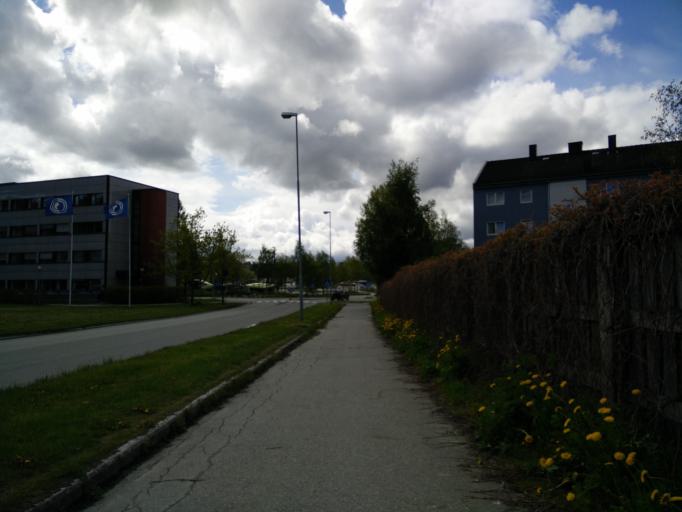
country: NO
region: Sor-Trondelag
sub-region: Trondheim
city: Trondheim
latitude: 63.4093
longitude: 10.4048
